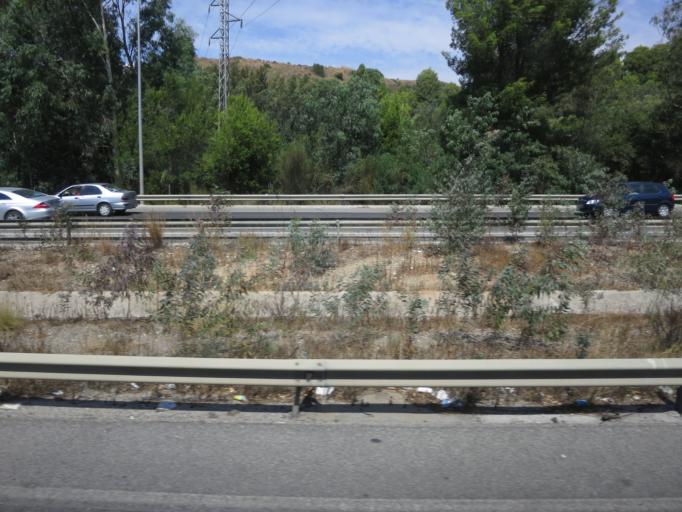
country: ES
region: Andalusia
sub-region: Provincia de Malaga
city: Marbella
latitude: 36.5124
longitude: -4.9454
